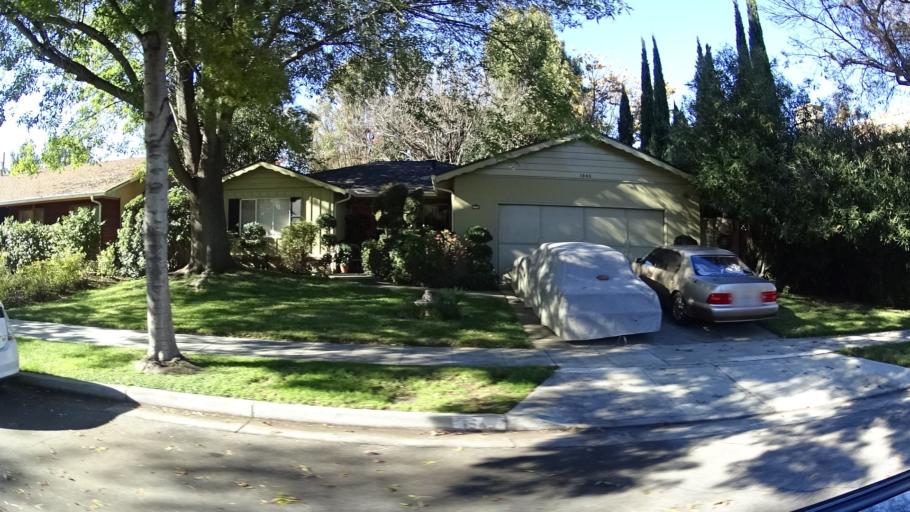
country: US
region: California
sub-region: Santa Clara County
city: Cupertino
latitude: 37.3414
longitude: -121.9980
